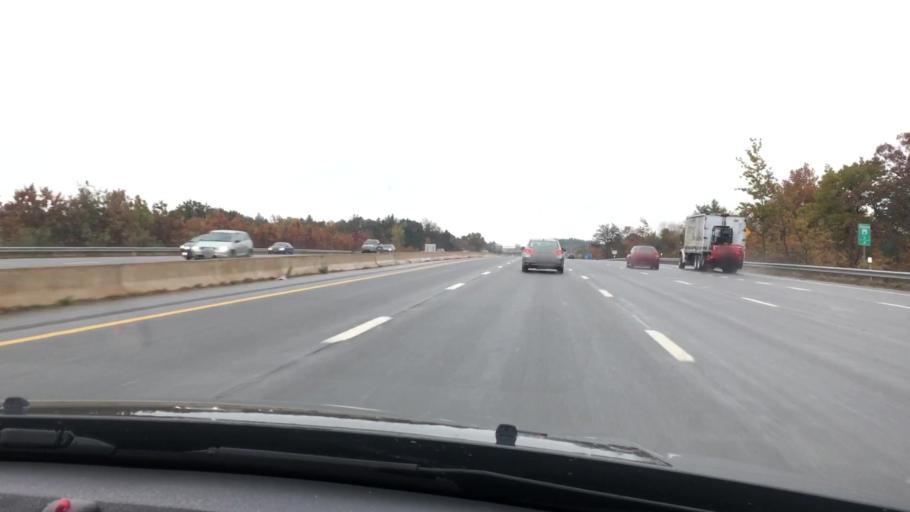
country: US
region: New Hampshire
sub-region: Hillsborough County
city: Nashua
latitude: 42.7599
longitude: -71.4934
